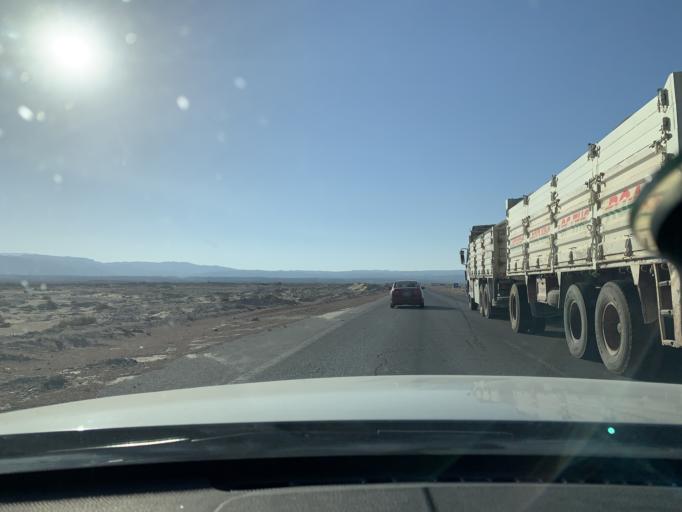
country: EG
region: As Suways
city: Ain Sukhna
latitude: 28.8889
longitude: 32.6506
